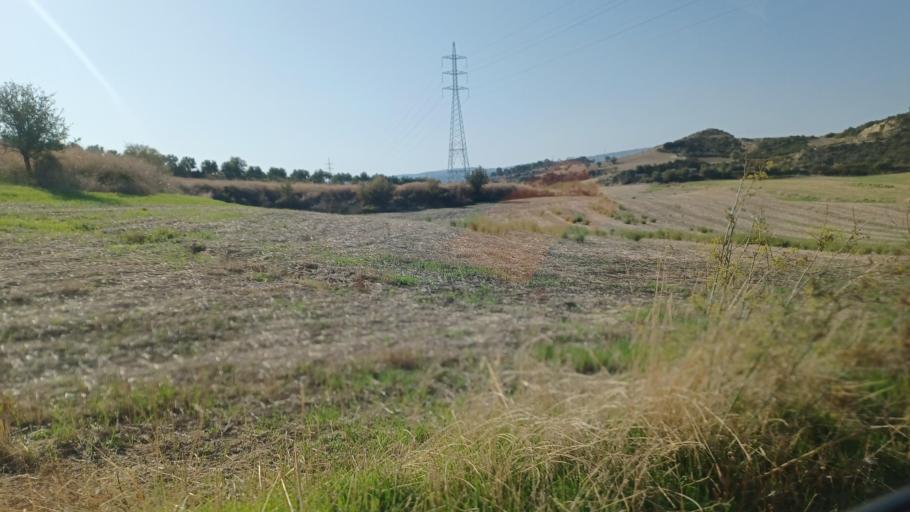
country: CY
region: Pafos
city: Polis
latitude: 35.0176
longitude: 32.4447
